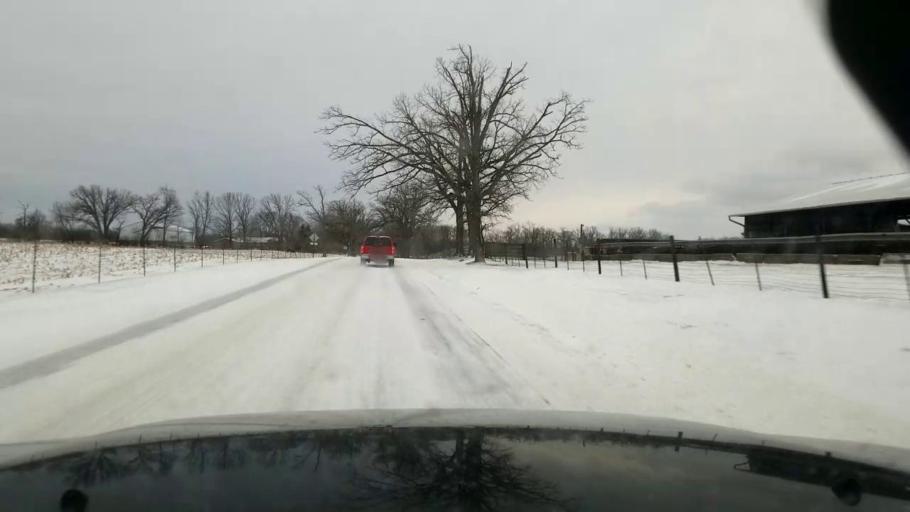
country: US
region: Michigan
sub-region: Jackson County
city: Spring Arbor
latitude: 42.1659
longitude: -84.5003
